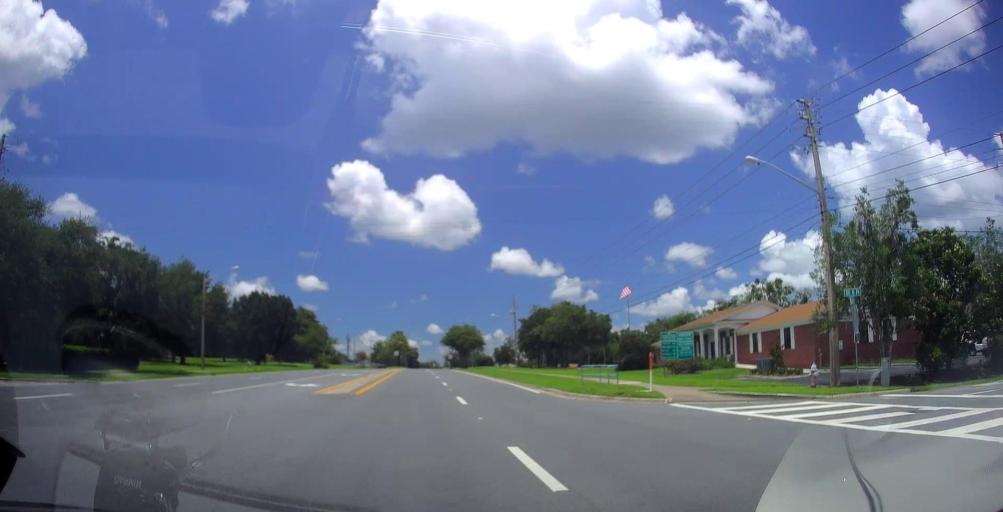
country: US
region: Florida
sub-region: Marion County
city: Ocala
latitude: 29.1811
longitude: -82.1031
